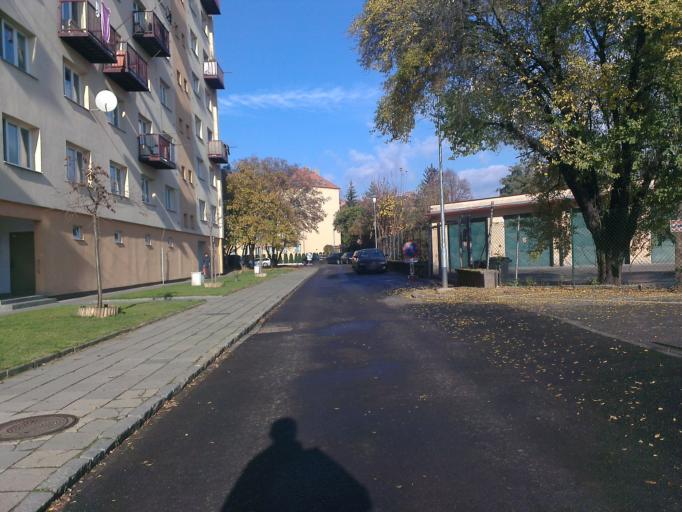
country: CZ
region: South Moravian
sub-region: Mesto Brno
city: Brno
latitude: 49.1781
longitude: 16.5990
